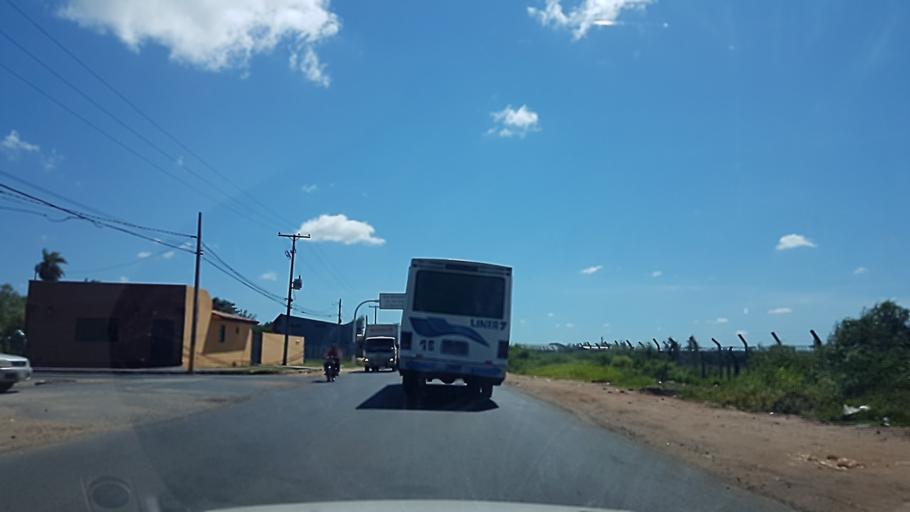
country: PY
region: Central
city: Limpio
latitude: -25.2136
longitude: -57.5150
